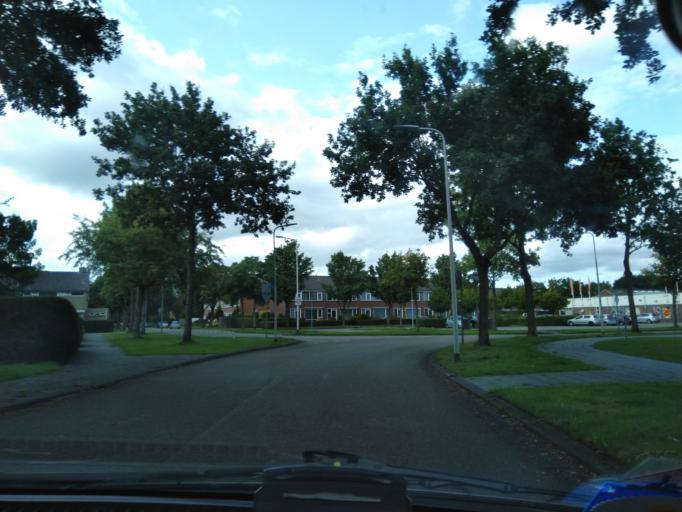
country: NL
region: Drenthe
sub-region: Gemeente Assen
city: Assen
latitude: 53.0061
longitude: 6.5401
